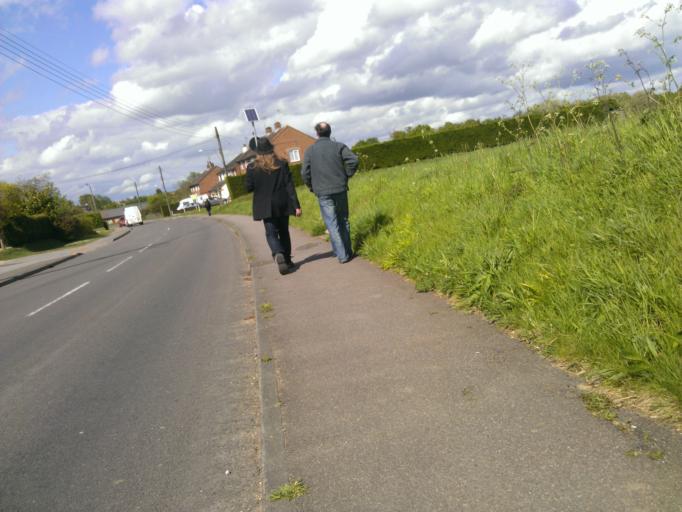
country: GB
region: England
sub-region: Essex
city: Eight Ash Green
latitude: 51.8729
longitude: 0.7985
